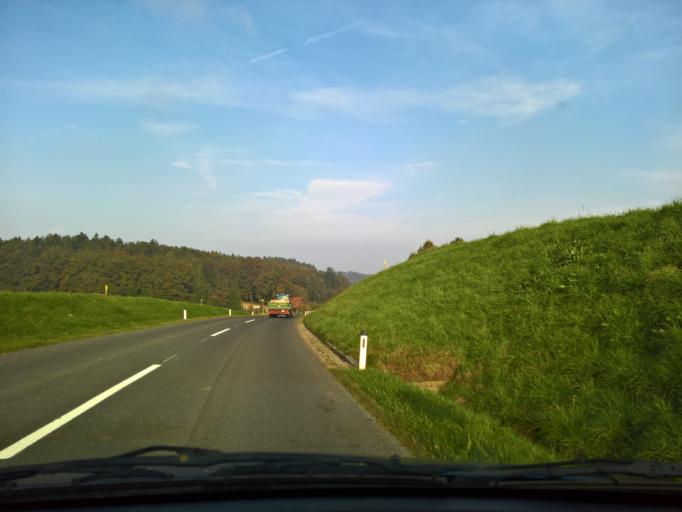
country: AT
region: Styria
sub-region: Politischer Bezirk Leibnitz
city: Pistorf
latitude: 46.7664
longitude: 15.3519
